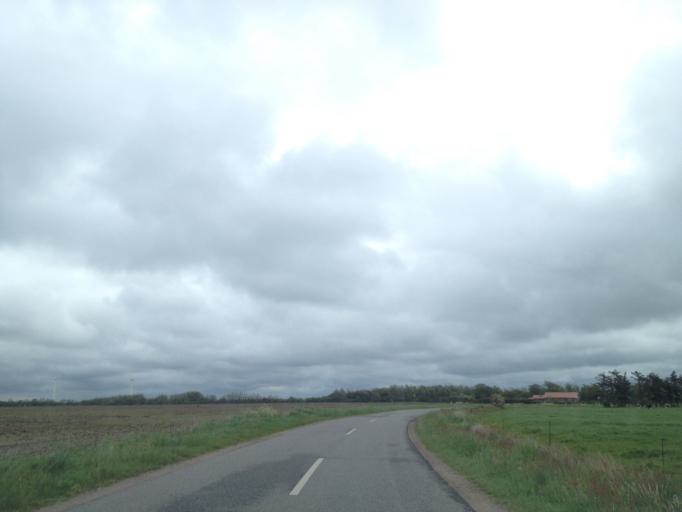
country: DK
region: South Denmark
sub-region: Tonder Kommune
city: Sherrebek
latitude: 55.1007
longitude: 8.7371
